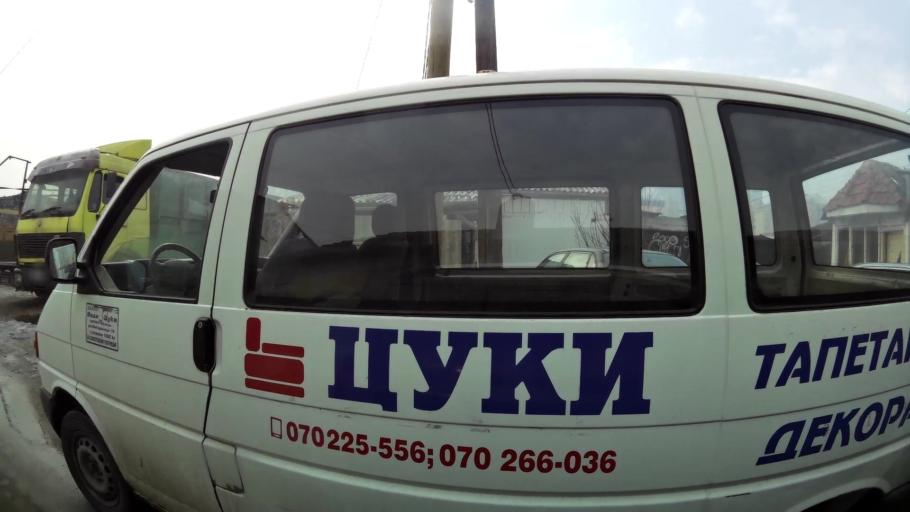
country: MK
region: Karpos
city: Skopje
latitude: 41.9928
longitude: 21.4528
